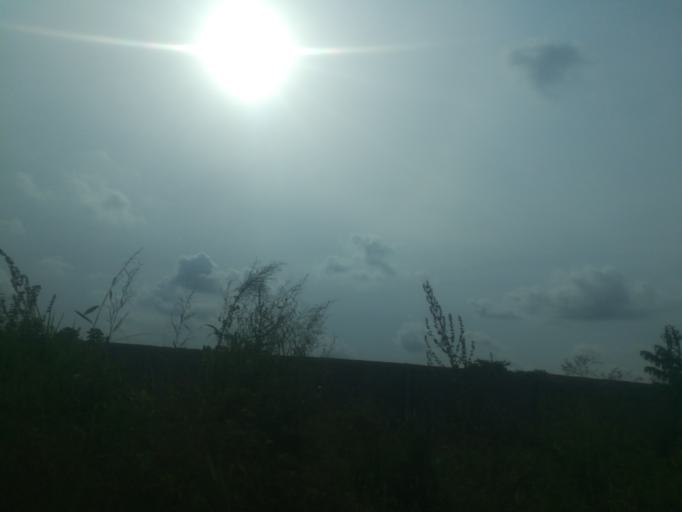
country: NG
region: Ogun
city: Ayetoro
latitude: 7.3361
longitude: 3.0624
